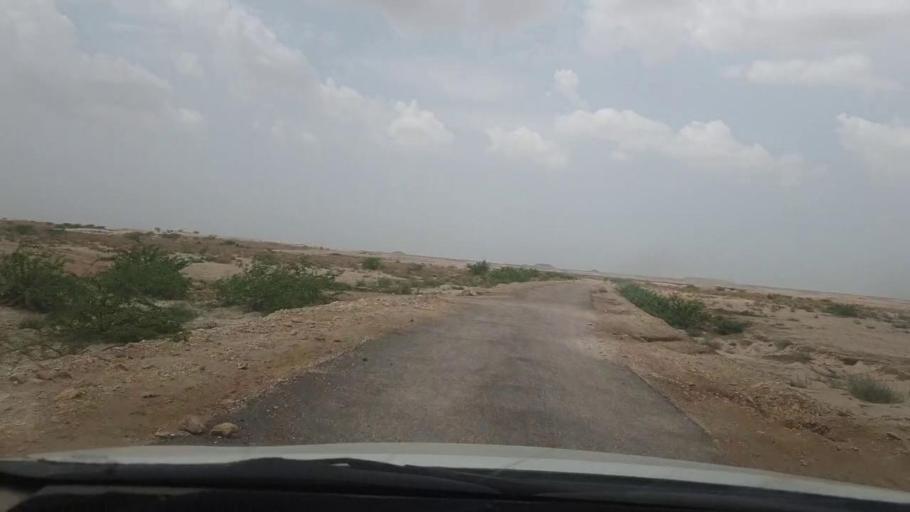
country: PK
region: Sindh
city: Khairpur
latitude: 27.3987
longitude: 68.9725
